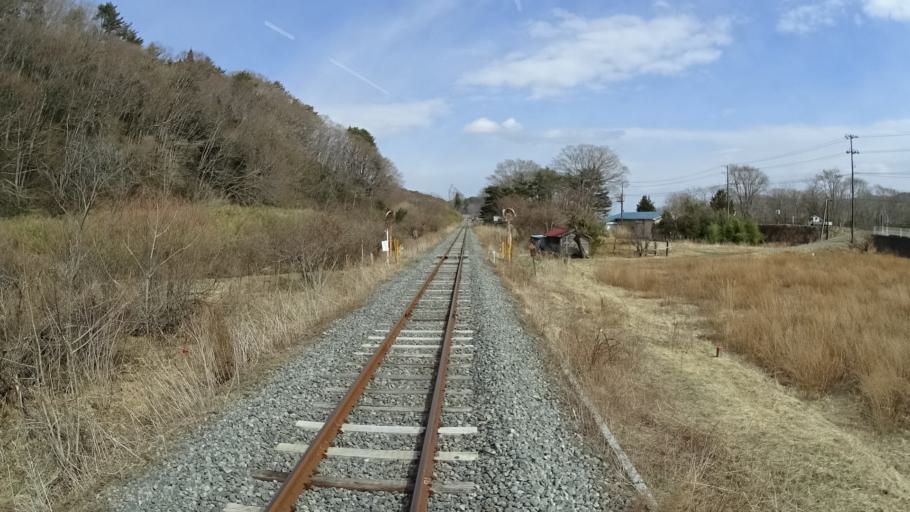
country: JP
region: Iwate
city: Miyako
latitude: 39.5697
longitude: 141.9320
